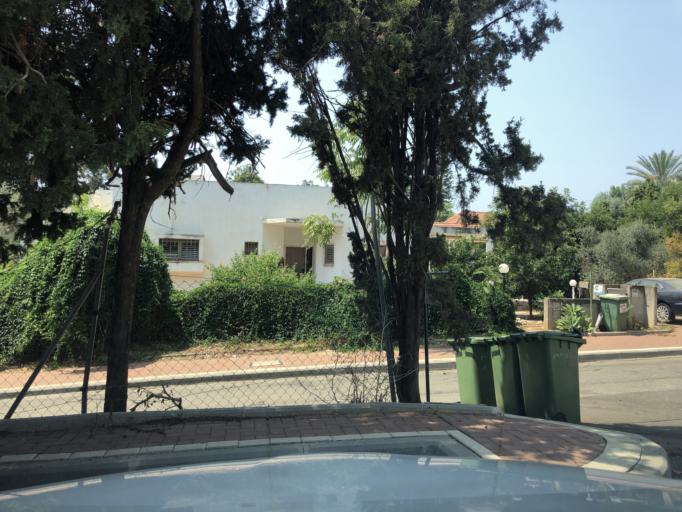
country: IL
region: Central District
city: Ganne Tiqwa
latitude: 32.0679
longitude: 34.8809
